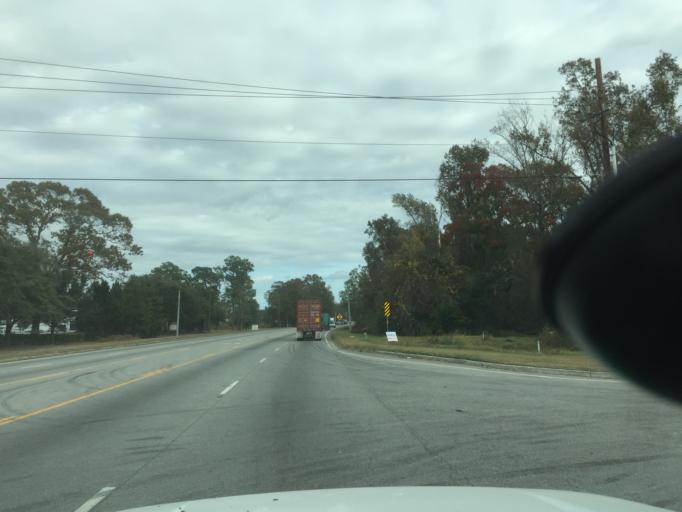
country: US
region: Georgia
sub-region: Chatham County
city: Garden City
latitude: 32.1159
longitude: -81.1923
